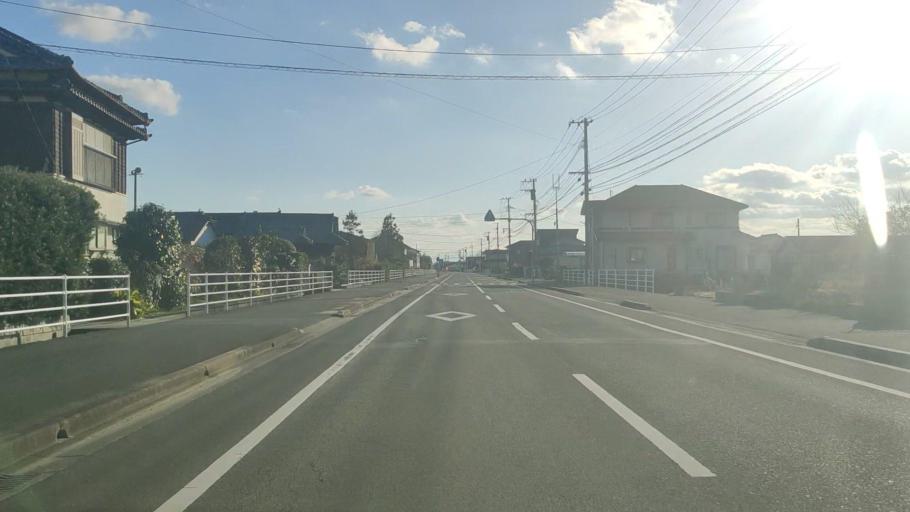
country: JP
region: Saga Prefecture
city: Saga-shi
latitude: 33.3146
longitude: 130.2659
